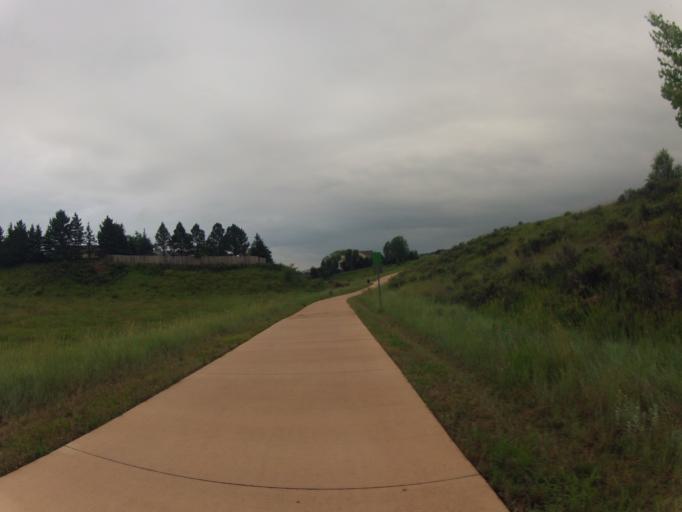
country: US
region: Colorado
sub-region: Larimer County
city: Fort Collins
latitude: 40.5306
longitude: -105.1243
